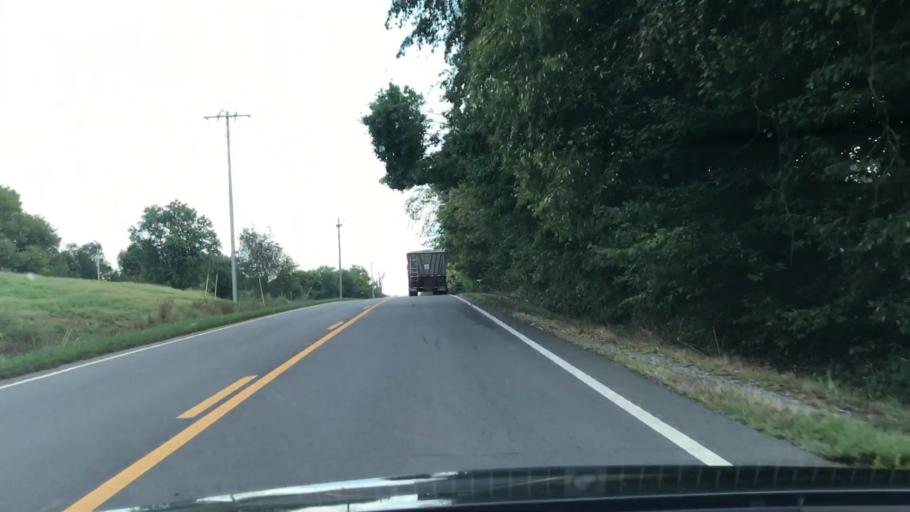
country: US
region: Tennessee
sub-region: Robertson County
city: Springfield
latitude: 36.6347
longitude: -86.9718
